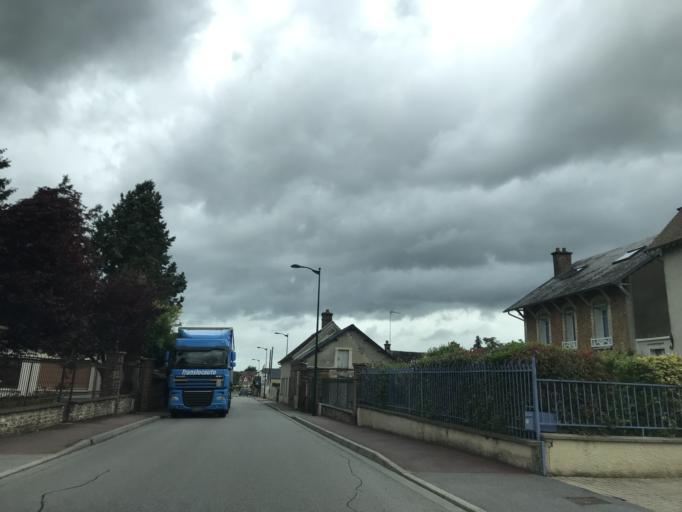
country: FR
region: Haute-Normandie
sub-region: Departement de l'Eure
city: La Couture-Boussey
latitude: 48.8971
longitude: 1.4110
